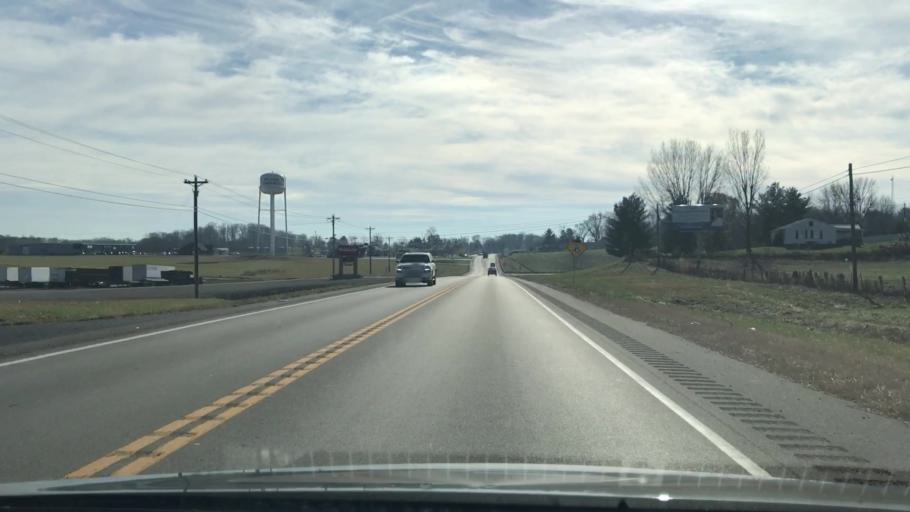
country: US
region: Kentucky
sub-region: Monroe County
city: Tompkinsville
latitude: 36.7297
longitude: -85.6875
